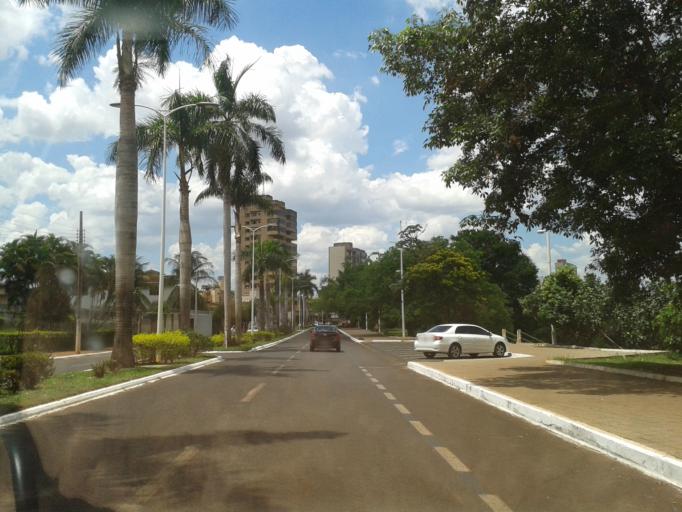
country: BR
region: Goias
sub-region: Itumbiara
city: Itumbiara
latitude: -18.4150
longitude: -49.2125
